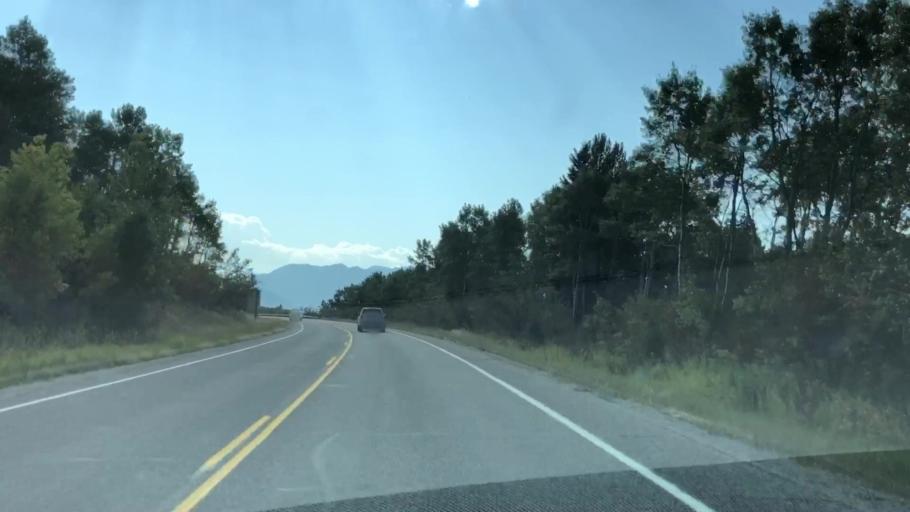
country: US
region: Wyoming
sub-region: Teton County
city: Hoback
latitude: 43.2098
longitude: -111.0581
